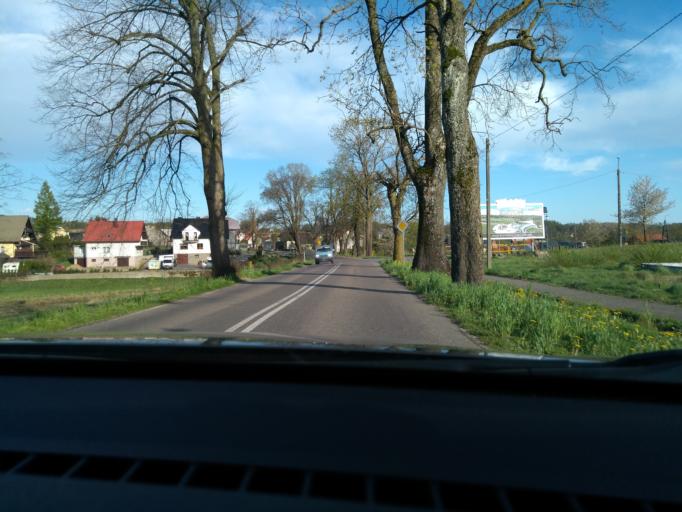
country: PL
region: Pomeranian Voivodeship
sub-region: Powiat kartuski
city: Suleczyno
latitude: 54.3264
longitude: 17.7896
